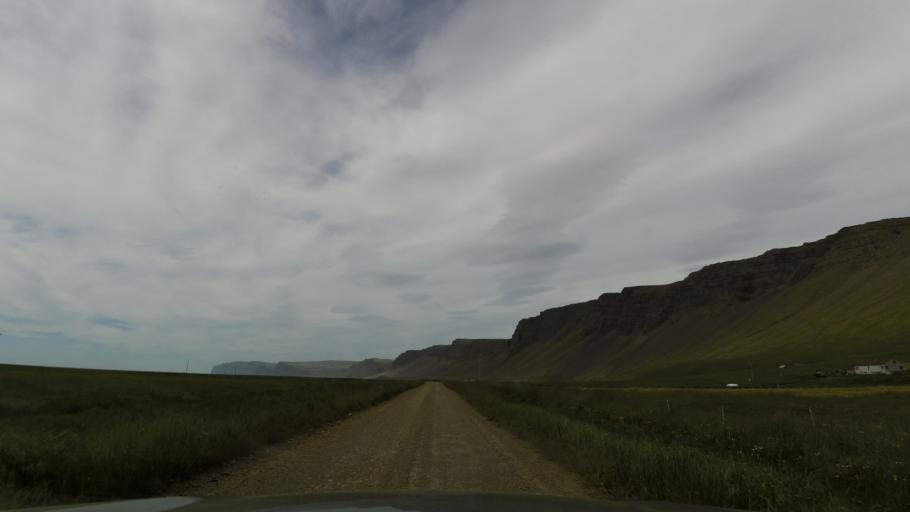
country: IS
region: West
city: Olafsvik
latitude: 65.4853
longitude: -24.0590
